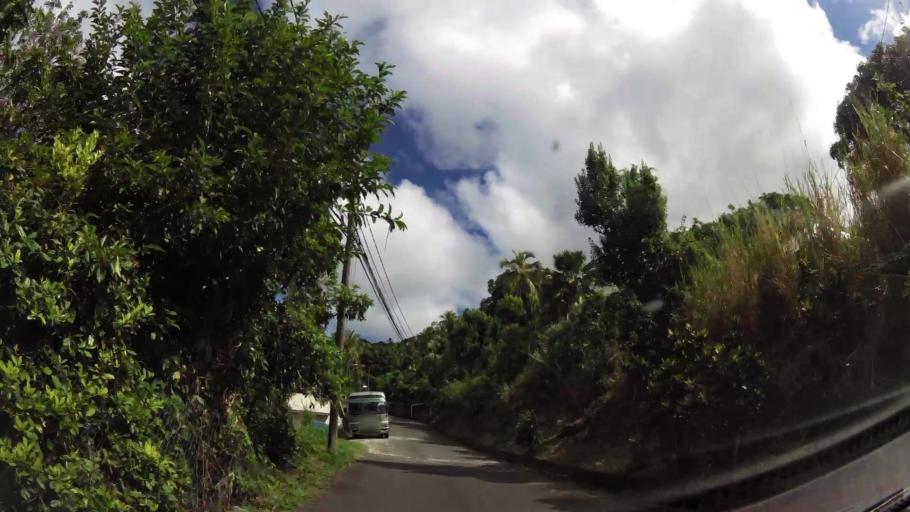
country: DM
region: Saint John
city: Portsmouth
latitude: 15.6146
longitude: -61.4640
